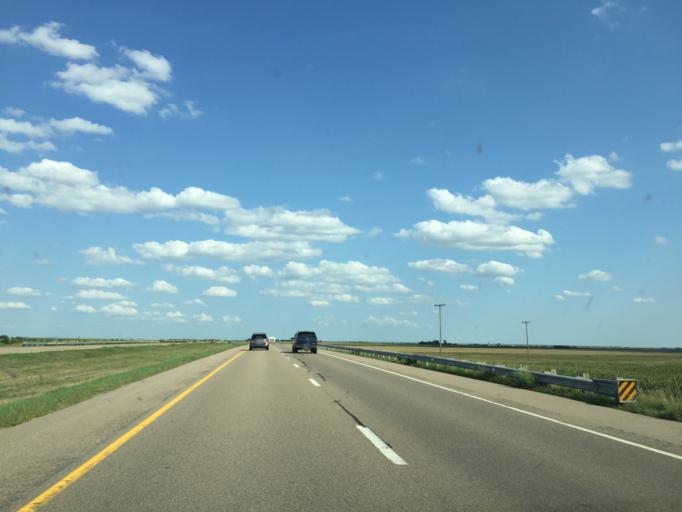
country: US
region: Kansas
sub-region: Gove County
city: Gove
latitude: 39.0411
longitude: -100.2060
